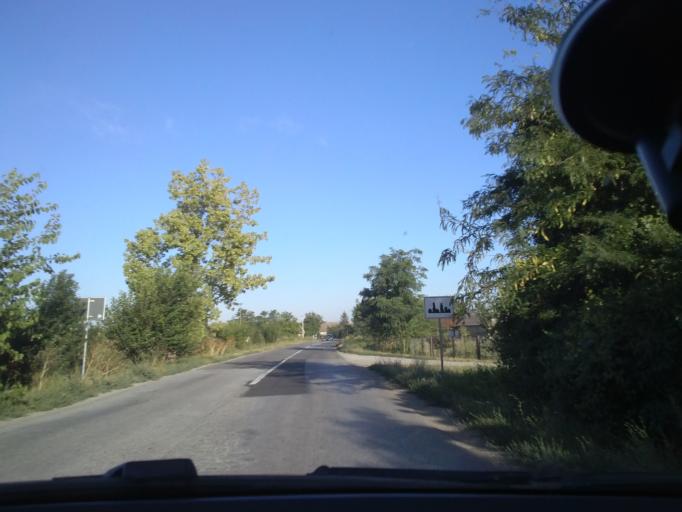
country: RS
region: Autonomna Pokrajina Vojvodina
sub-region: Zapadnobacki Okrug
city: Odzaci
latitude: 45.4592
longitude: 19.3224
